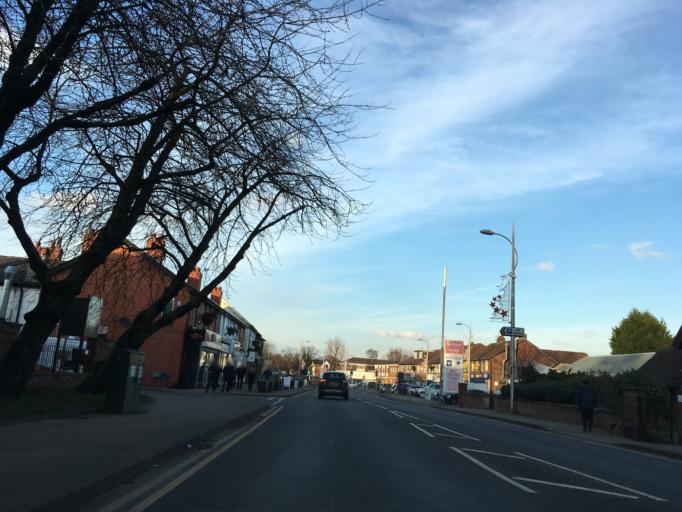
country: GB
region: England
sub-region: Cheshire East
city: Wilmslow
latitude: 53.3483
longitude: -2.2152
